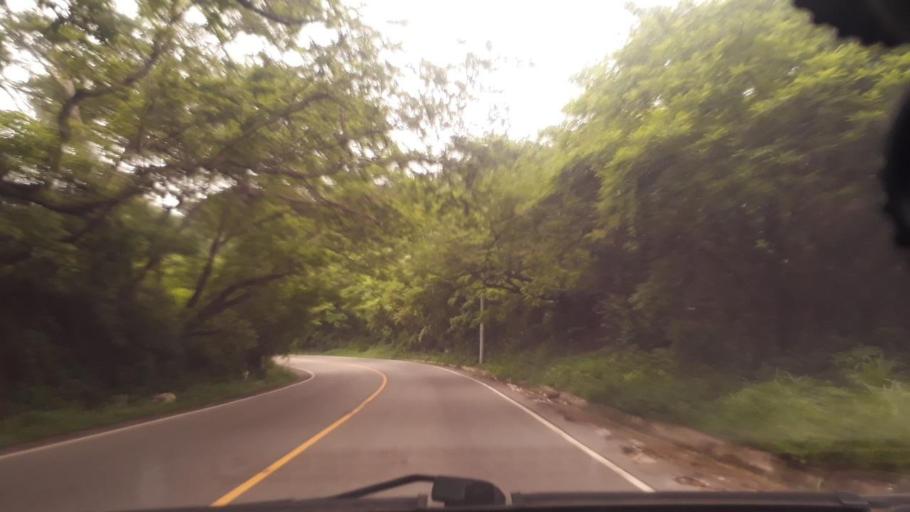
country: GT
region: Chiquimula
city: San Jacinto
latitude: 14.6484
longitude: -89.4823
